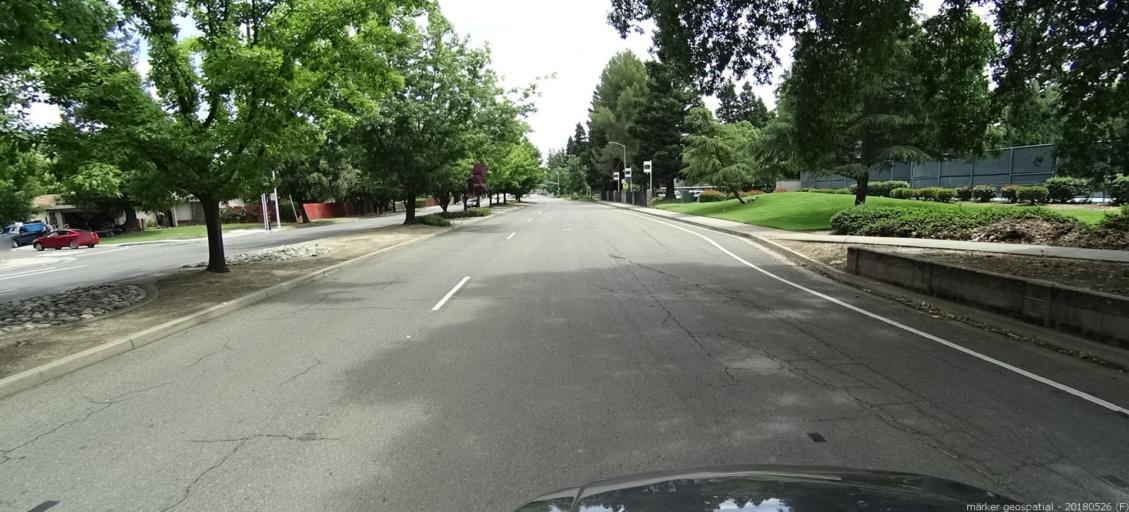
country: US
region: California
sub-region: Sacramento County
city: Sacramento
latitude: 38.6127
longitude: -121.5038
